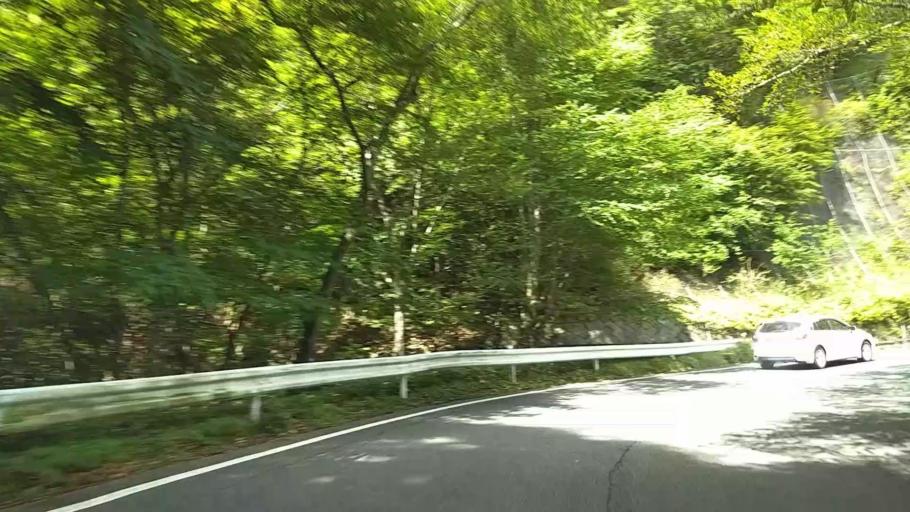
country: JP
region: Tochigi
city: Nikko
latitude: 36.7308
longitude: 139.5161
